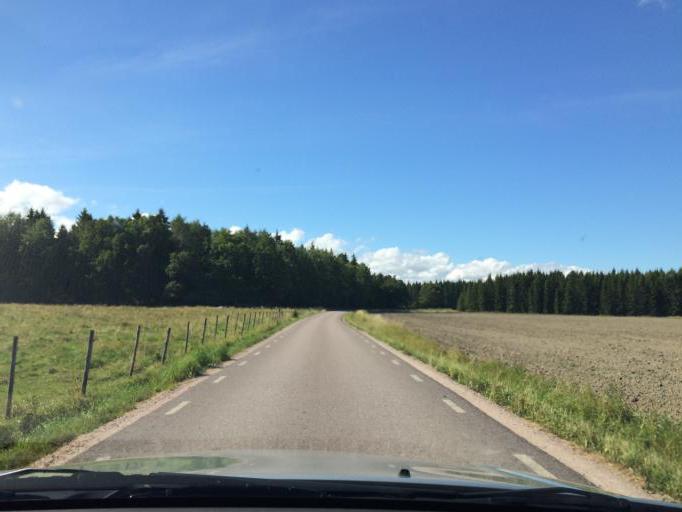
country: SE
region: Soedermanland
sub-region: Eskilstuna Kommun
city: Kvicksund
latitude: 59.5019
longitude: 16.3713
